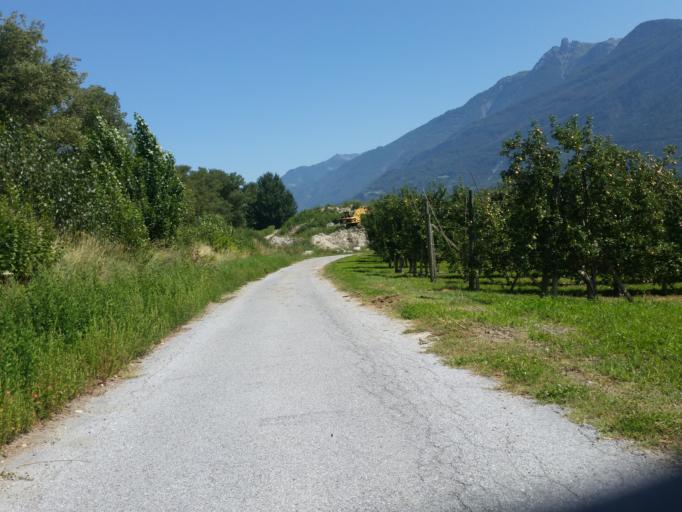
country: CH
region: Valais
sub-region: Martigny District
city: Fully
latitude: 46.1244
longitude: 7.0905
